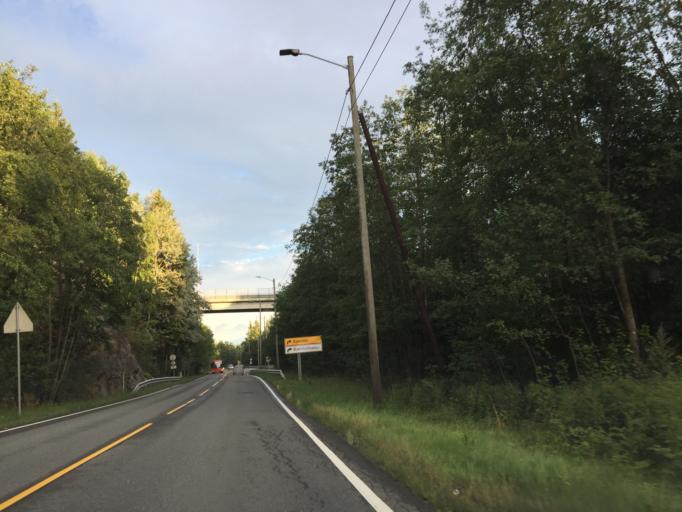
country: NO
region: Akershus
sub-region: Oppegard
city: Kolbotn
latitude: 59.8385
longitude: 10.8324
